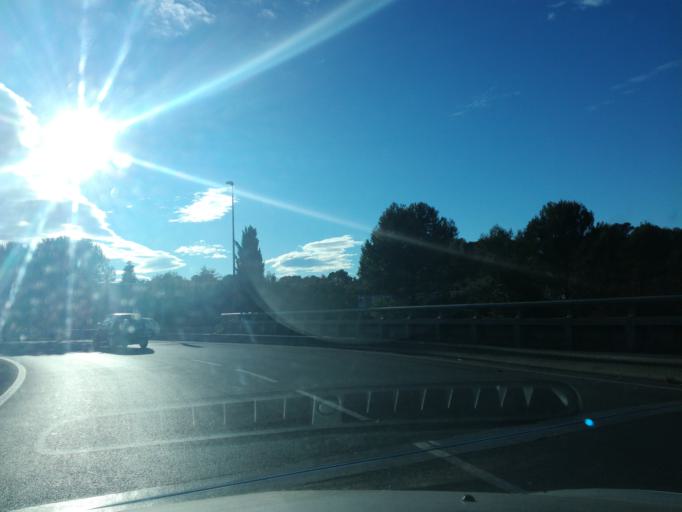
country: FR
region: Provence-Alpes-Cote d'Azur
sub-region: Departement des Alpes-Maritimes
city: Mouans-Sartoux
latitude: 43.6122
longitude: 6.9675
